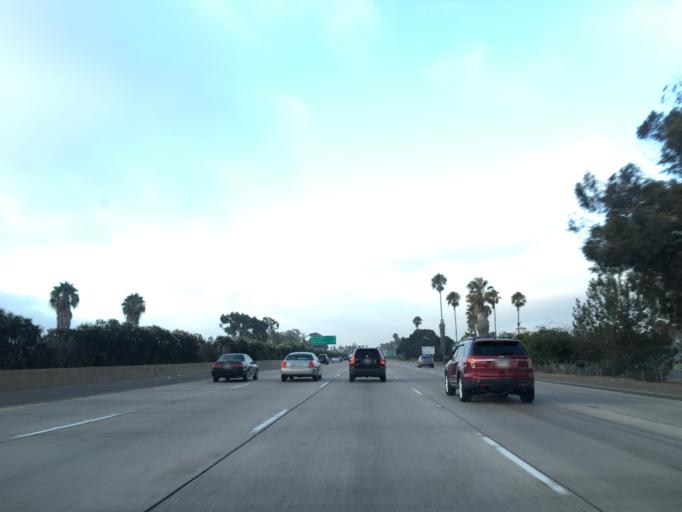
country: US
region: California
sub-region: San Diego County
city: San Diego
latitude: 32.7847
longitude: -117.2078
